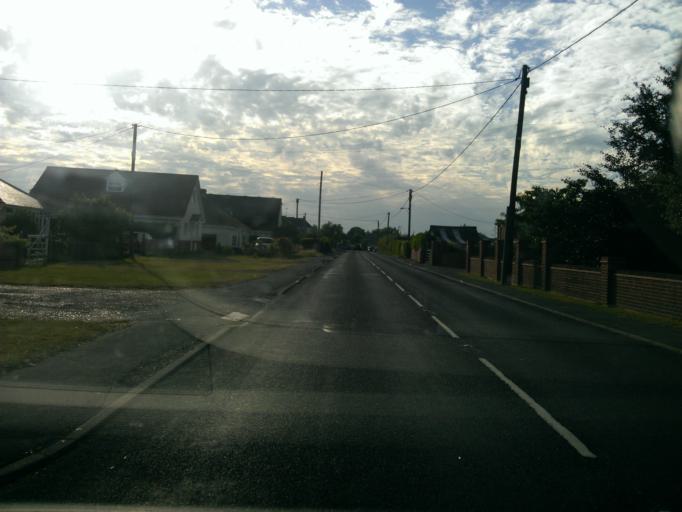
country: GB
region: England
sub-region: Essex
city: Little Clacton
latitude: 51.8435
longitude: 1.1258
